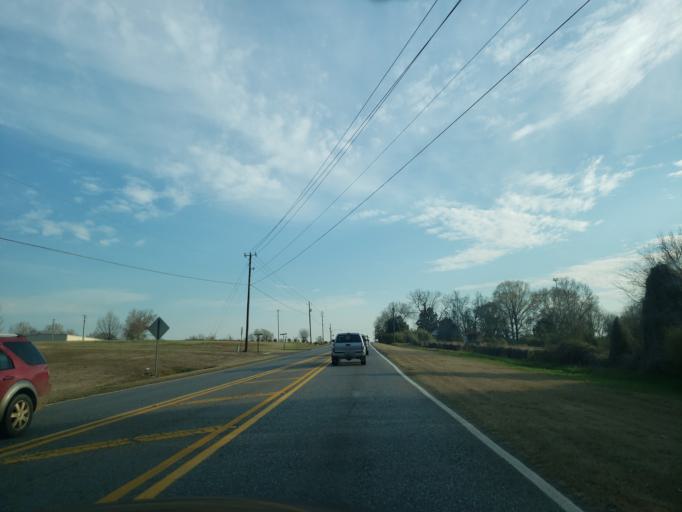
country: US
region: Alabama
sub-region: Hale County
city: Moundville
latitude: 32.9933
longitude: -87.6243
